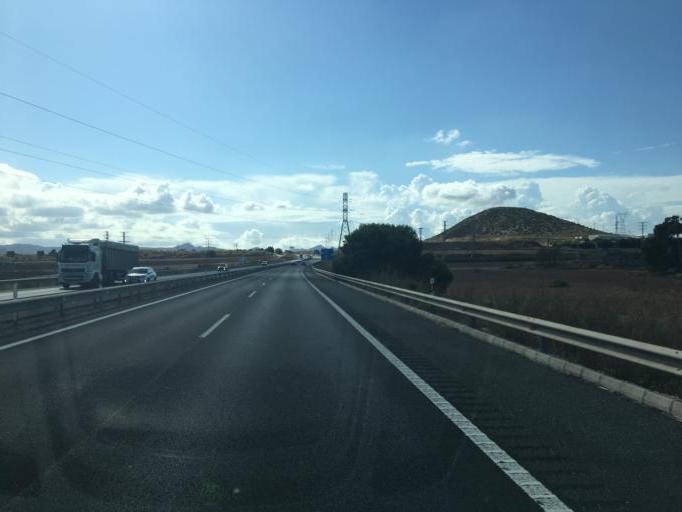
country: ES
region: Murcia
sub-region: Murcia
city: Cartagena
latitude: 37.6388
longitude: -0.9603
